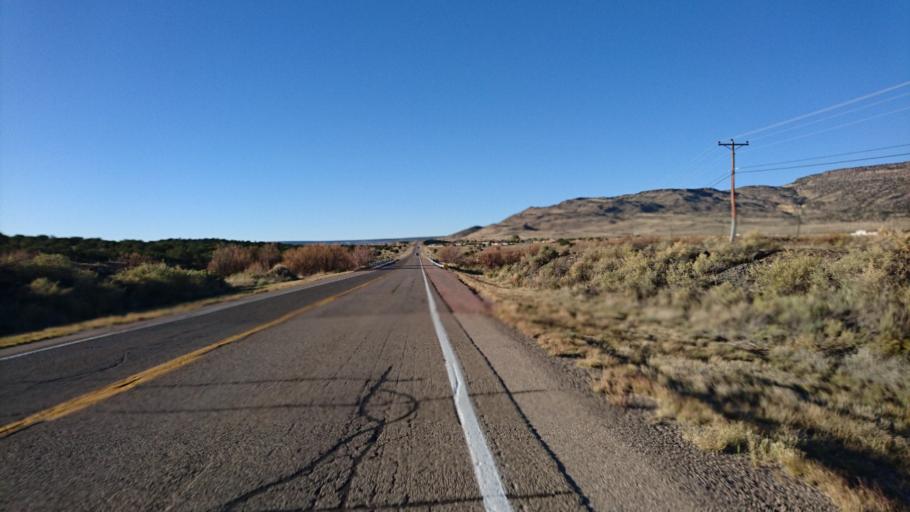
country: US
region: New Mexico
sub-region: Cibola County
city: Grants
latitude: 35.0965
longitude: -107.7728
